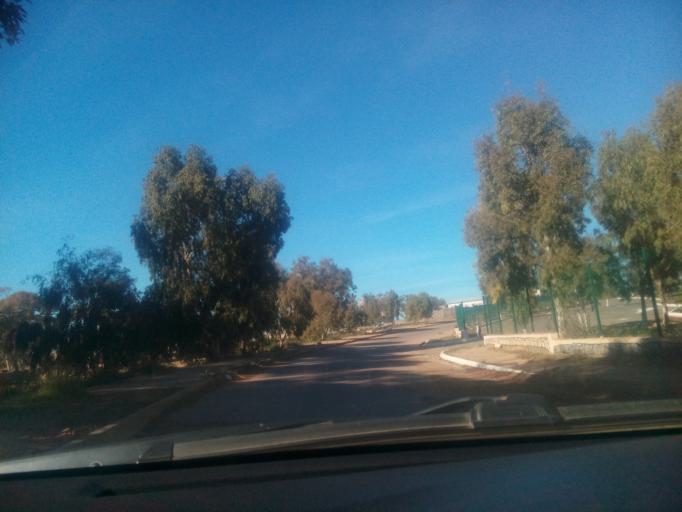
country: DZ
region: Oran
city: Bir el Djir
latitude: 35.7291
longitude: -0.5400
